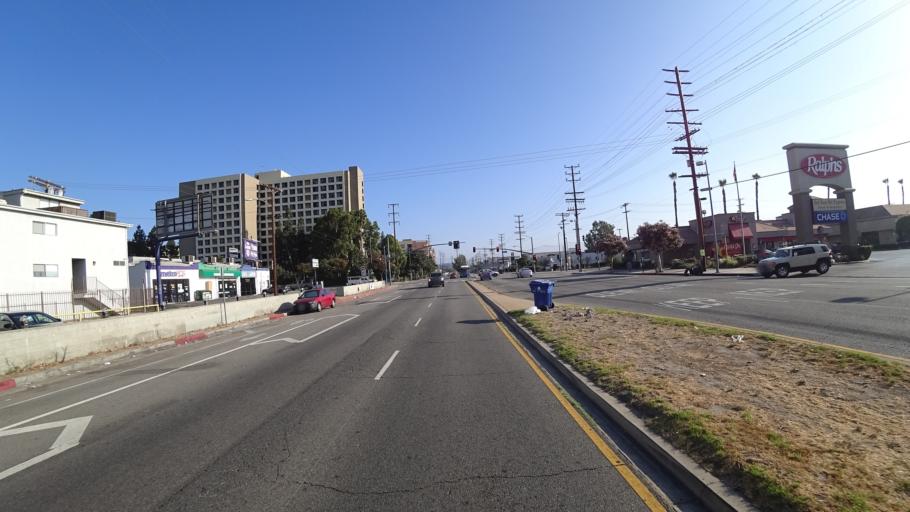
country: US
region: California
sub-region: Los Angeles County
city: North Hollywood
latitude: 34.1642
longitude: -118.3705
